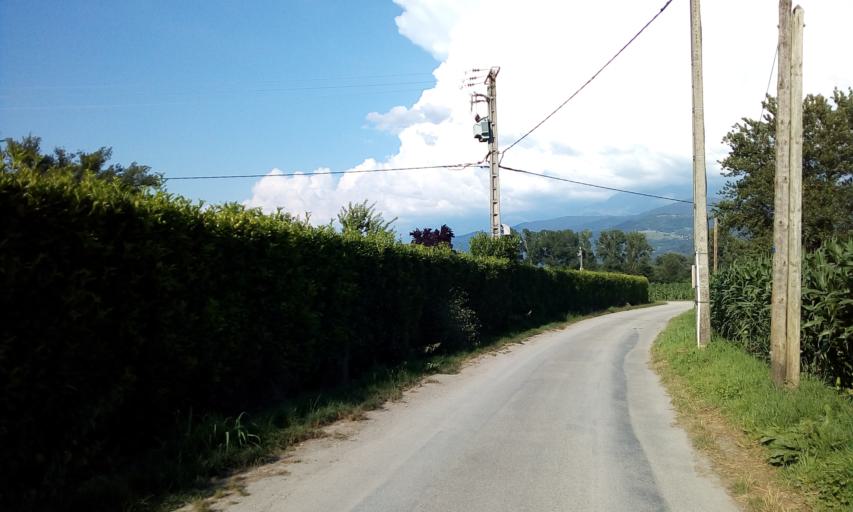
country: FR
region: Rhone-Alpes
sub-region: Departement de l'Isere
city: Gieres
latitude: 45.1977
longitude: 5.7842
